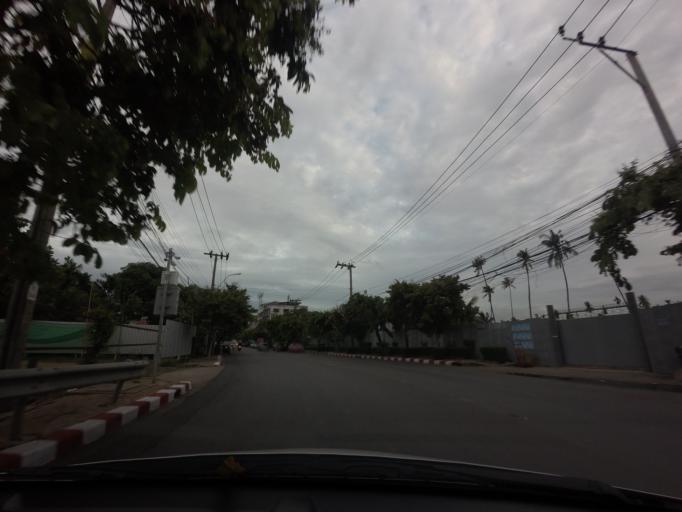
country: TH
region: Bangkok
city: Chom Thong
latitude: 13.6875
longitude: 100.4632
